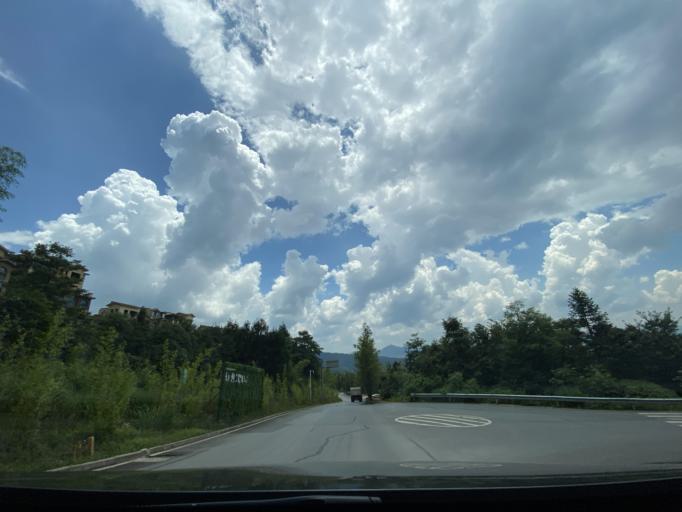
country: CN
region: Guizhou Sheng
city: Changqi
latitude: 28.5331
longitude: 105.9672
